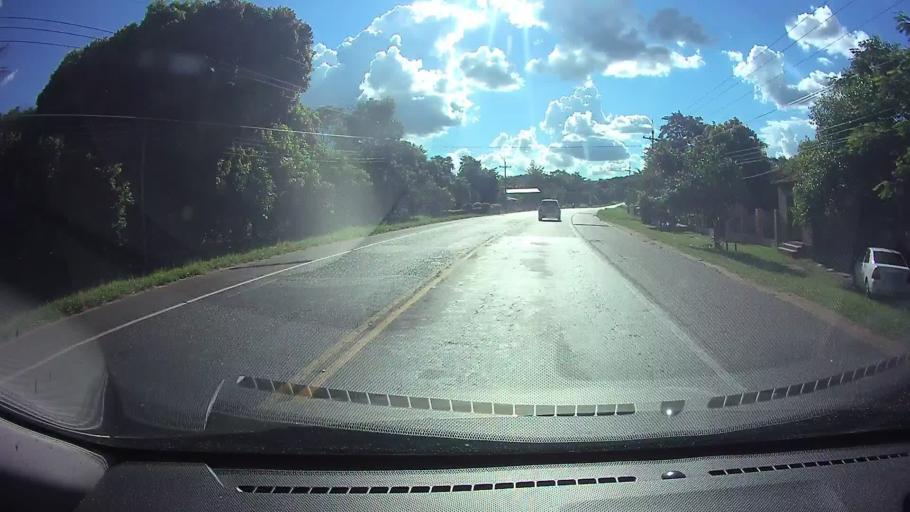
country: PY
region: Cordillera
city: Eusebio Ayala
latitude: -25.3823
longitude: -57.0078
